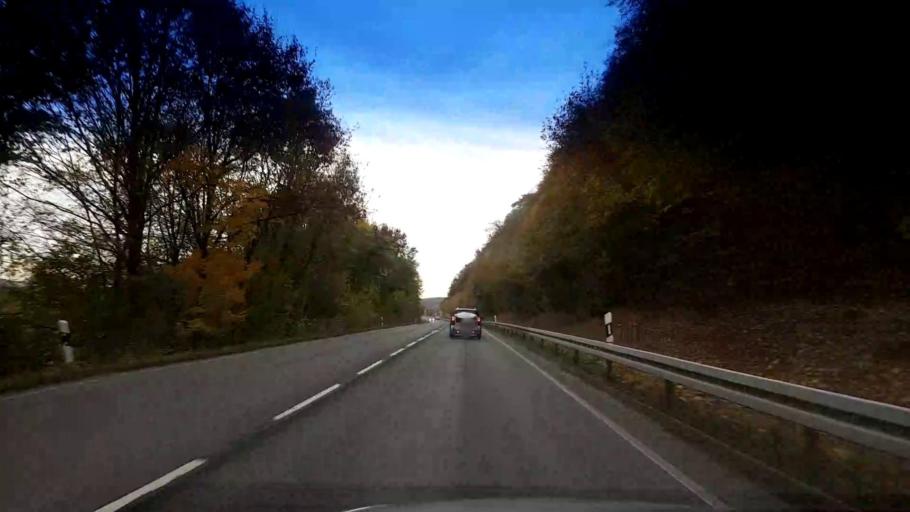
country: DE
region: Bavaria
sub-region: Regierungsbezirk Unterfranken
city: Stettfeld
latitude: 49.9535
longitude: 10.7173
